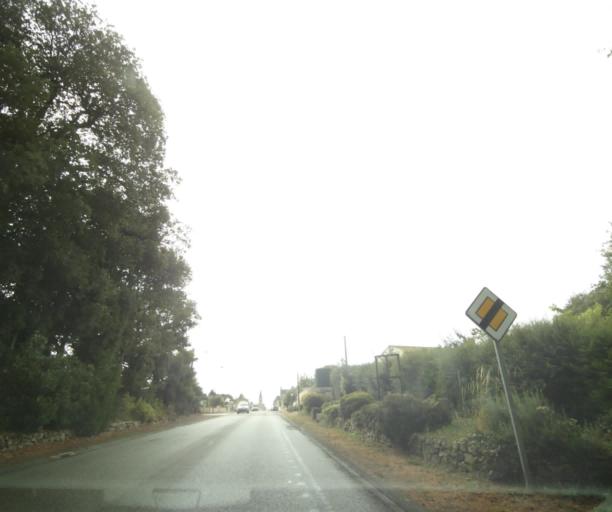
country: FR
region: Pays de la Loire
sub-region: Departement de la Vendee
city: Avrille
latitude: 46.4719
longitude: -1.5006
